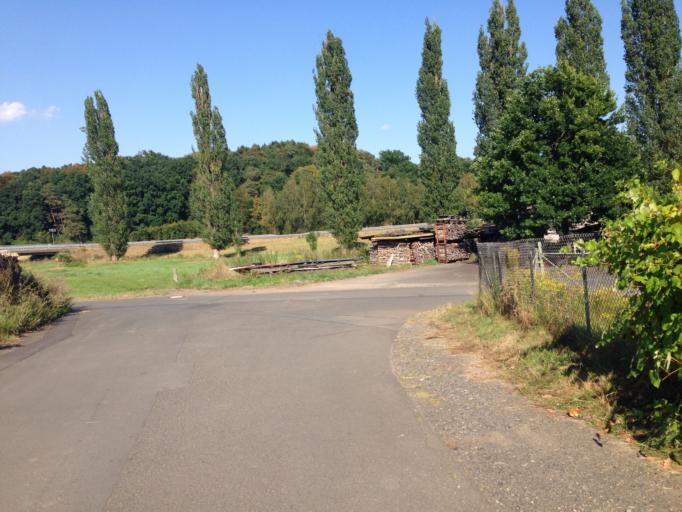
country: DE
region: Hesse
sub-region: Regierungsbezirk Giessen
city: Rabenau
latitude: 50.6498
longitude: 8.8942
